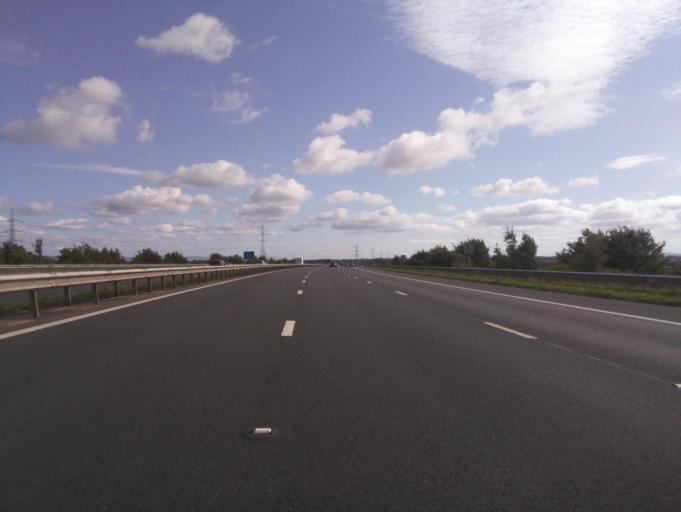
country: GB
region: Scotland
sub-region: Dumfries and Galloway
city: Gretna
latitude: 54.9899
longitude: -3.0423
